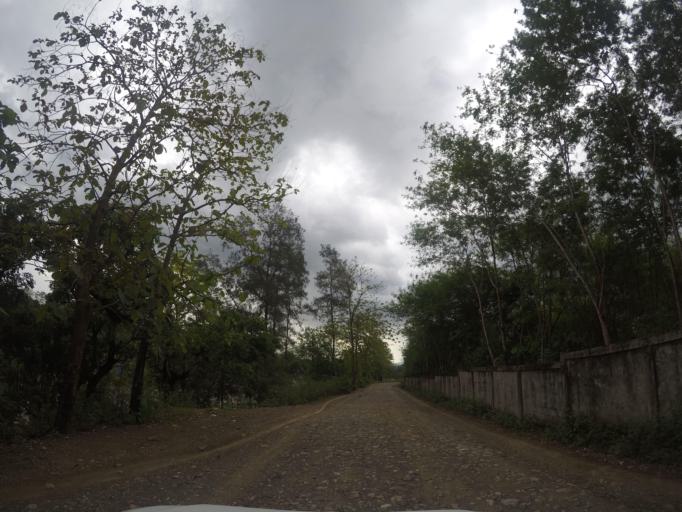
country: TL
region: Bobonaro
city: Maliana
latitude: -8.9745
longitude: 125.2235
